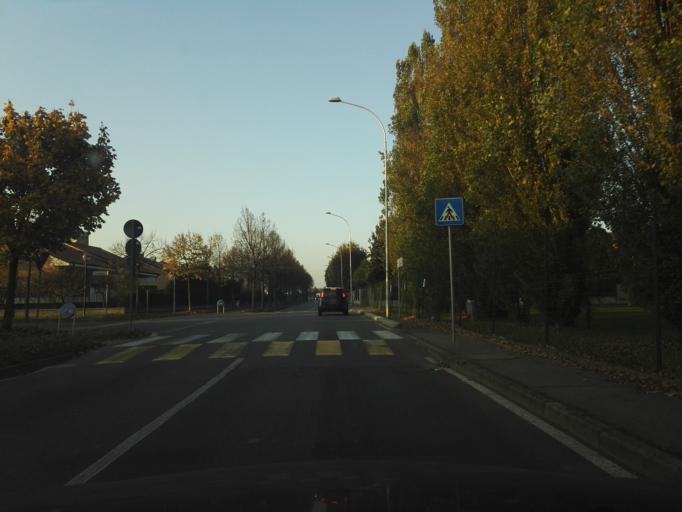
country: IT
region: Lombardy
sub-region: Citta metropolitana di Milano
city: Vigliano-Bettolino
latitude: 45.4335
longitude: 9.3474
